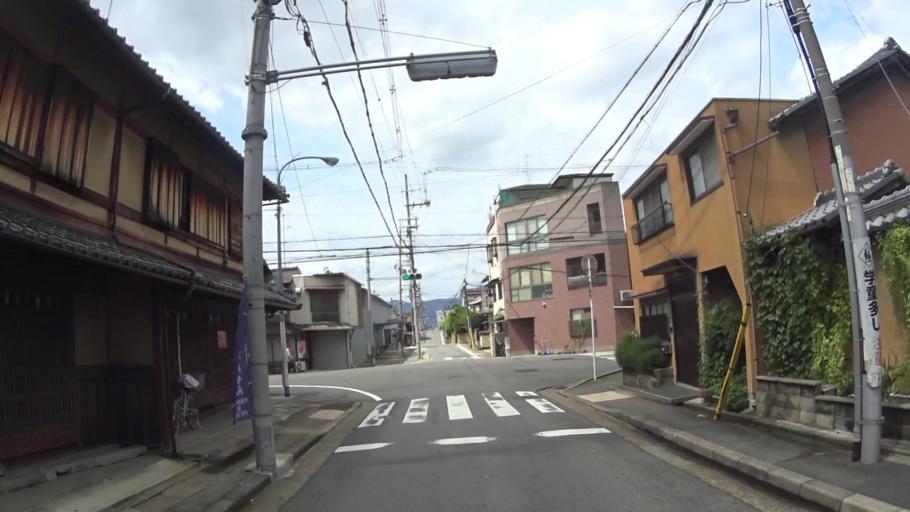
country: JP
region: Kyoto
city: Muko
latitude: 34.9647
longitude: 135.7428
